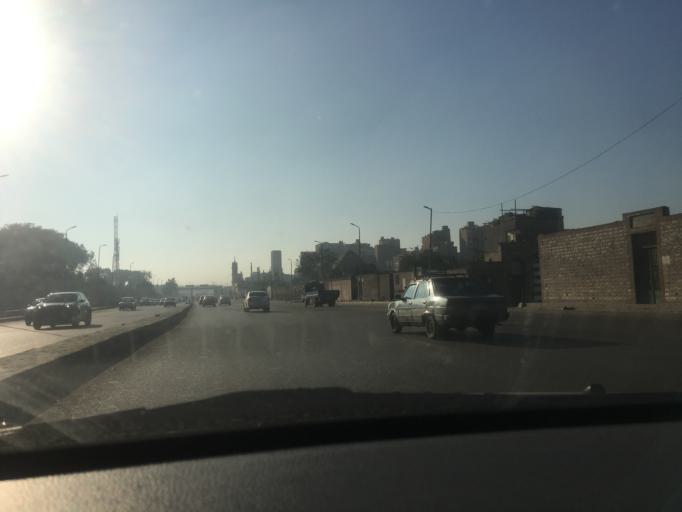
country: EG
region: Muhafazat al Qahirah
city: Cairo
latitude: 30.0169
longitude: 31.2650
